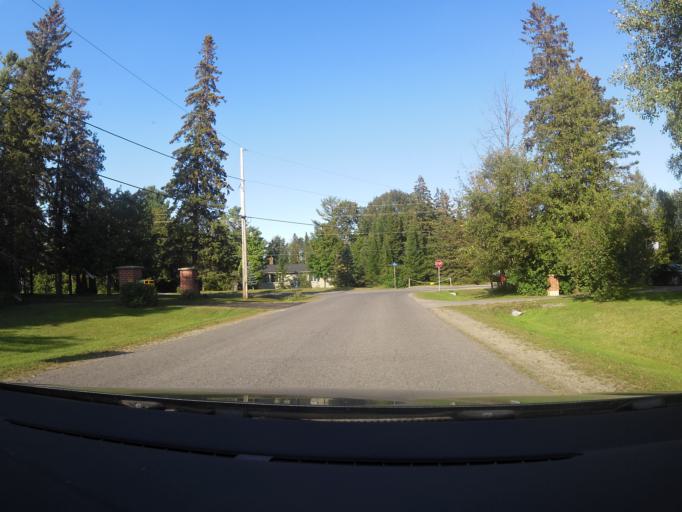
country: CA
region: Ontario
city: Carleton Place
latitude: 45.2854
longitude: -76.1047
